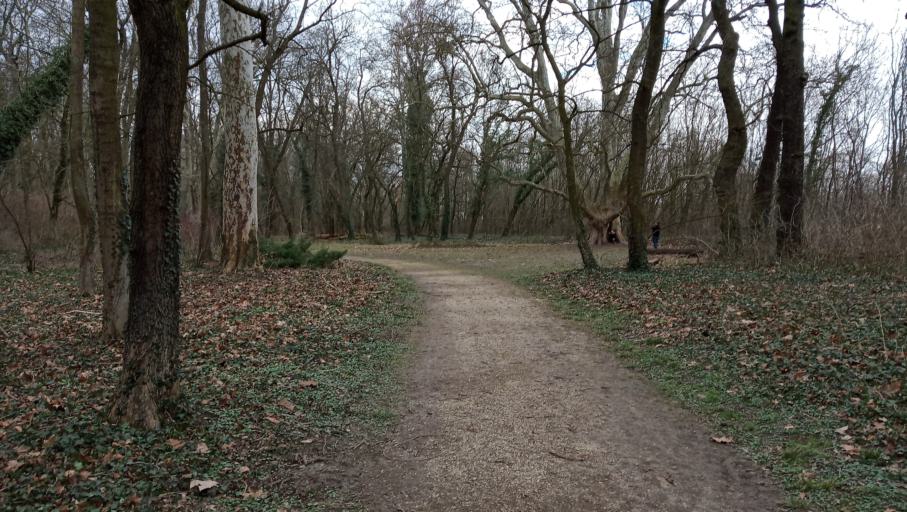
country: HU
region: Fejer
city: Bicske
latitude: 47.4251
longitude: 18.5951
